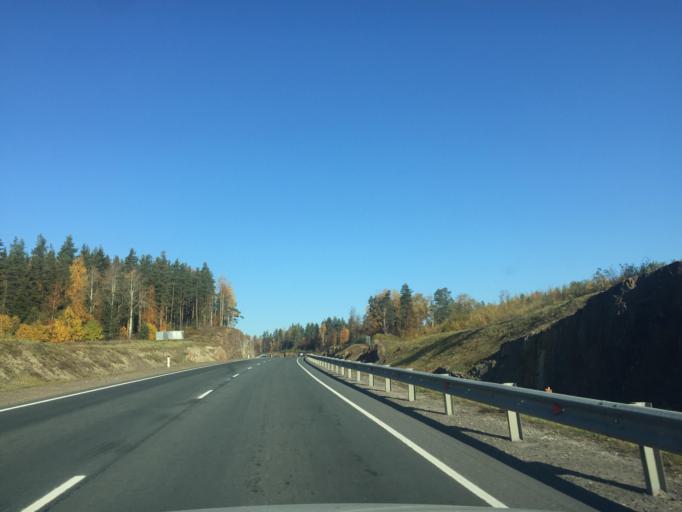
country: RU
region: Leningrad
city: Kuznechnoye
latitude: 61.2337
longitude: 29.7738
